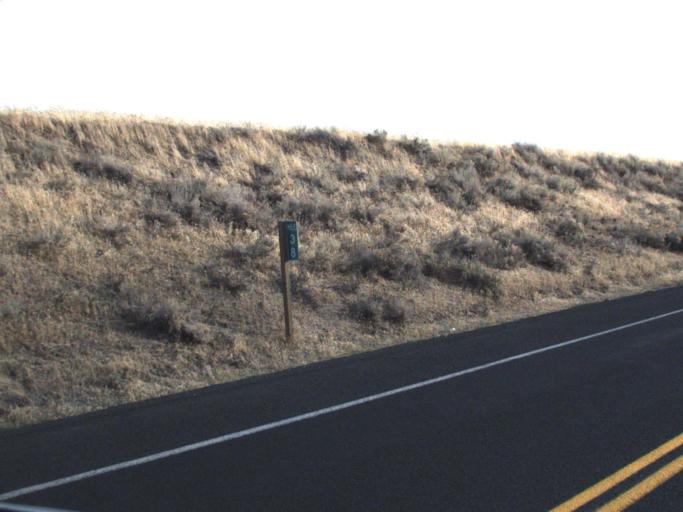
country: US
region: Washington
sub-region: Adams County
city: Ritzville
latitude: 47.0995
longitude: -118.6666
